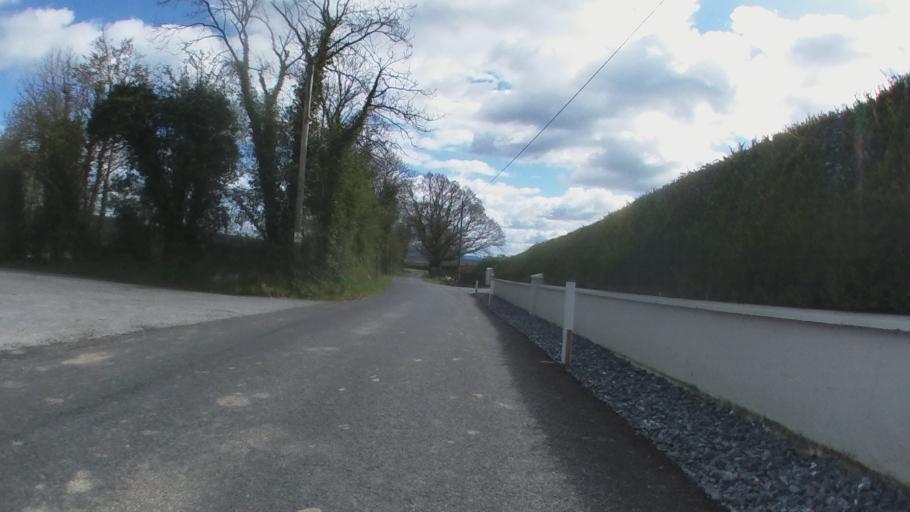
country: IE
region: Leinster
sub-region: Kilkenny
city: Kilkenny
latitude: 52.7050
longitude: -7.2091
